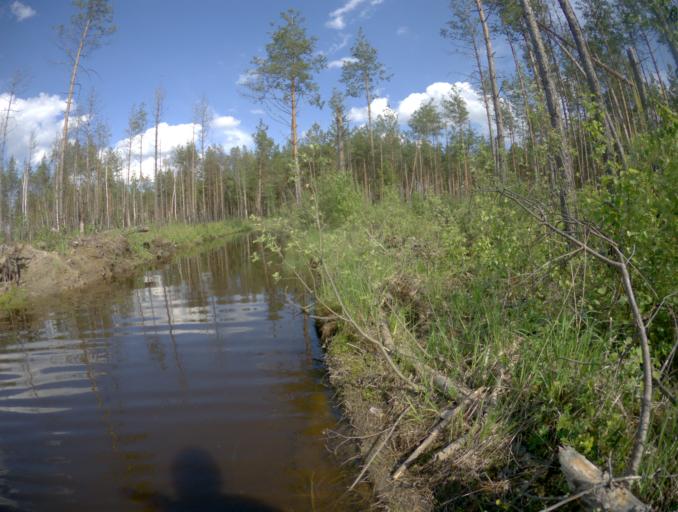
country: RU
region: Vladimir
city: Velikodvorskiy
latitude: 55.3171
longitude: 40.9220
